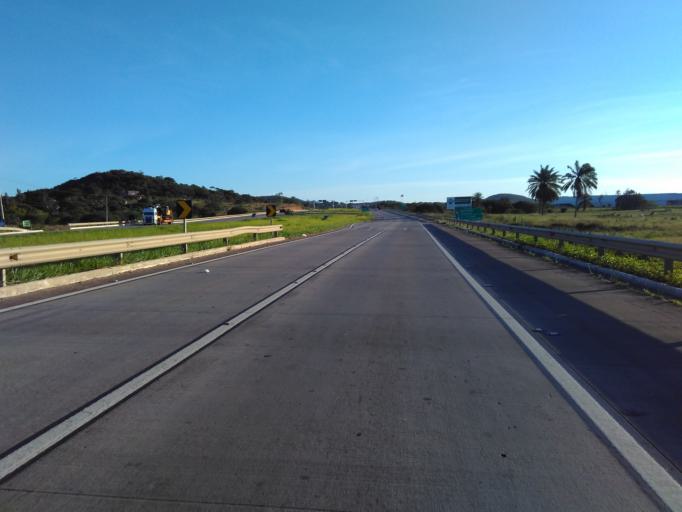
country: BR
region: Sergipe
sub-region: Nossa Senhora Do Socorro
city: Nossa Senhora do Socorro
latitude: -10.9170
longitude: -37.1665
